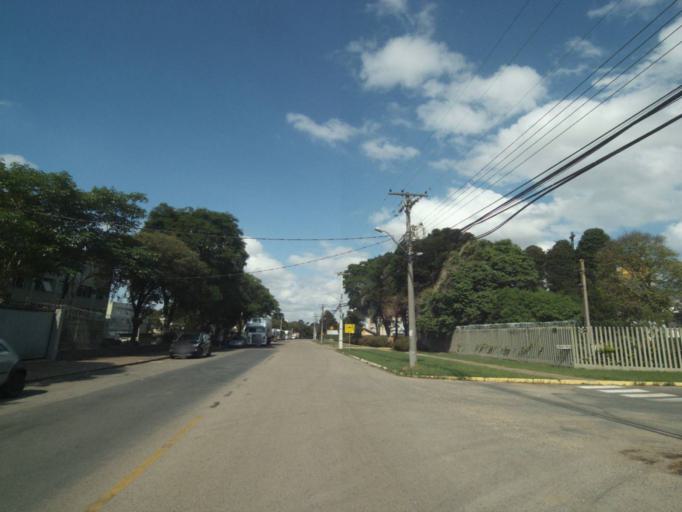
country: BR
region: Parana
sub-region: Curitiba
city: Curitiba
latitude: -25.4956
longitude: -49.3142
